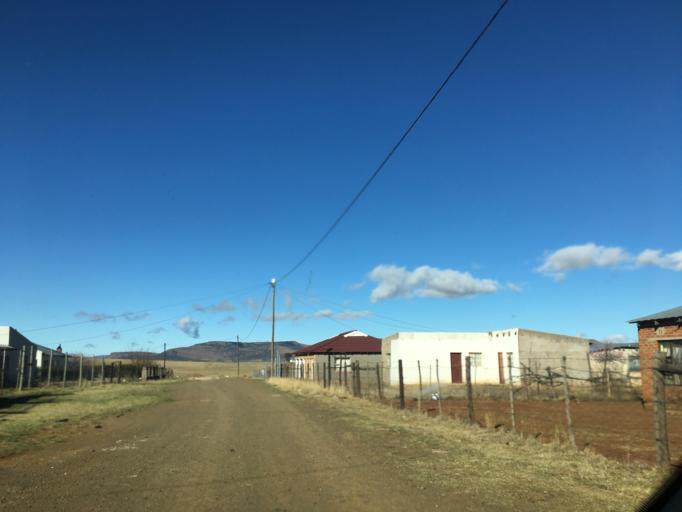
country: ZA
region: Eastern Cape
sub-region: Chris Hani District Municipality
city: Cala
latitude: -31.5391
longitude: 27.6966
